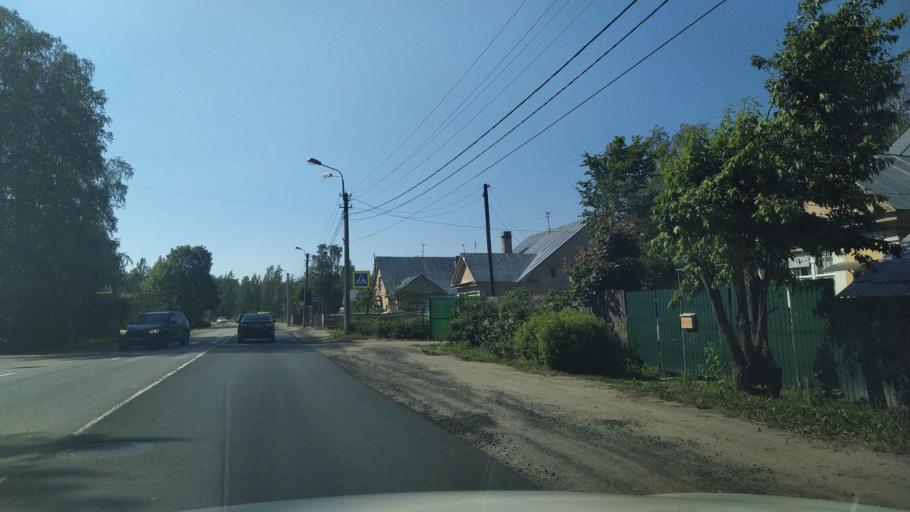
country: RU
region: St.-Petersburg
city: Beloostrov
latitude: 60.1461
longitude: 29.9973
